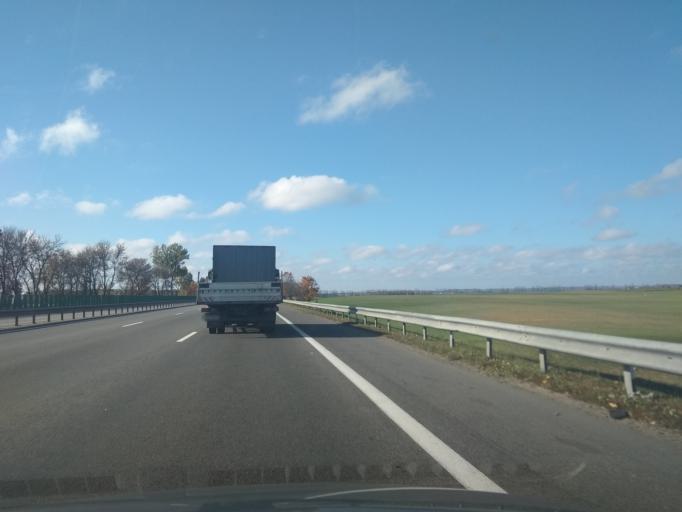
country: BY
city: Fanipol
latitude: 53.7259
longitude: 27.2702
